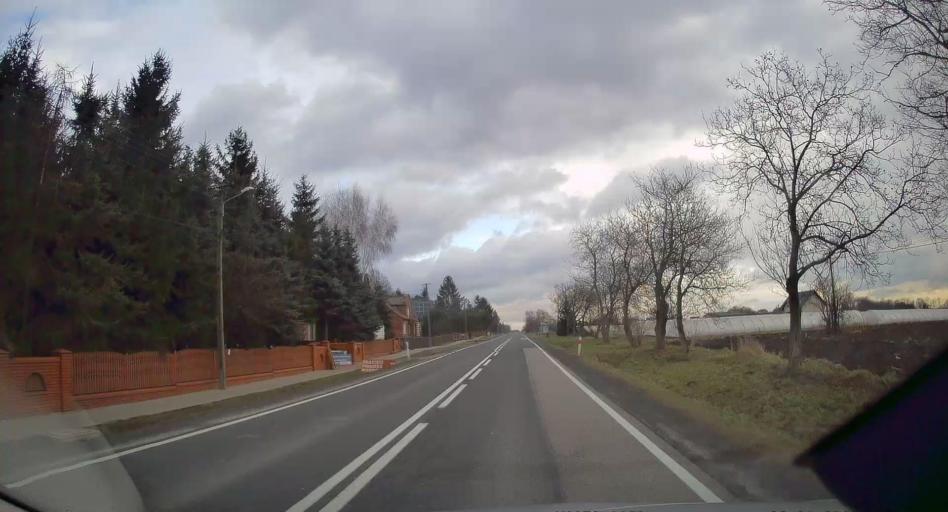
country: PL
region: Lesser Poland Voivodeship
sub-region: Powiat proszowicki
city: Nowe Brzesko
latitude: 50.1480
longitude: 20.4070
